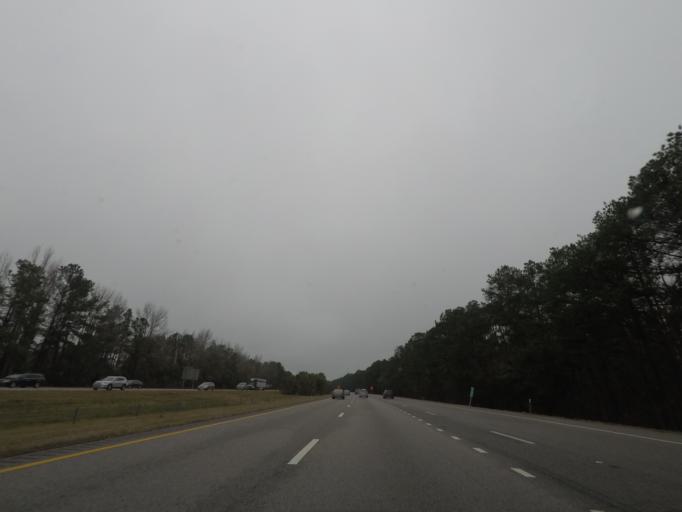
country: US
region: South Carolina
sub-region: Sumter County
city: East Sumter
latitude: 33.8983
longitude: -80.0951
